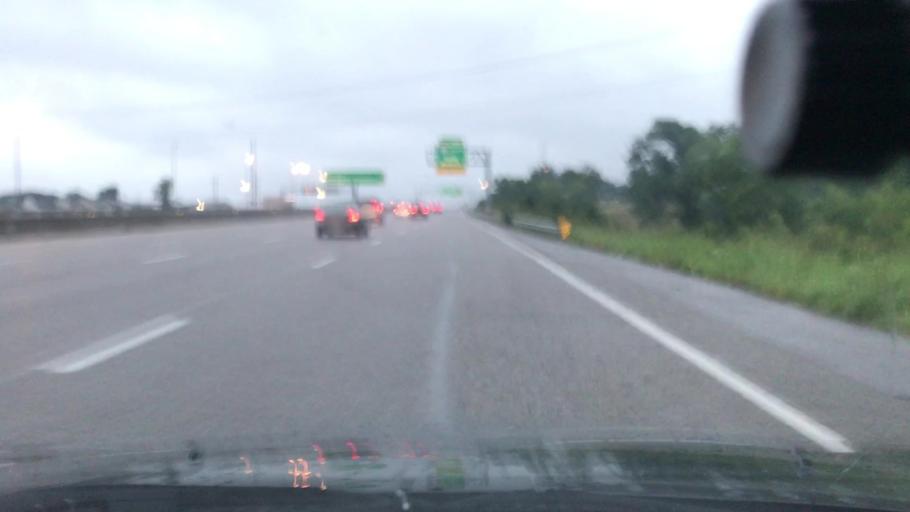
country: US
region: Missouri
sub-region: Saint Louis County
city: Maryland Heights
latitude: 38.6964
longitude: -90.4599
